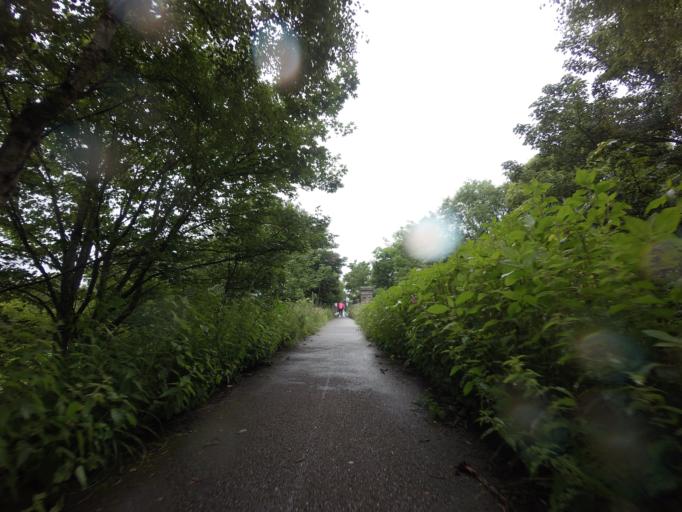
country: GB
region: Scotland
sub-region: Moray
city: Fochabers
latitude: 57.6628
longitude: -3.1014
